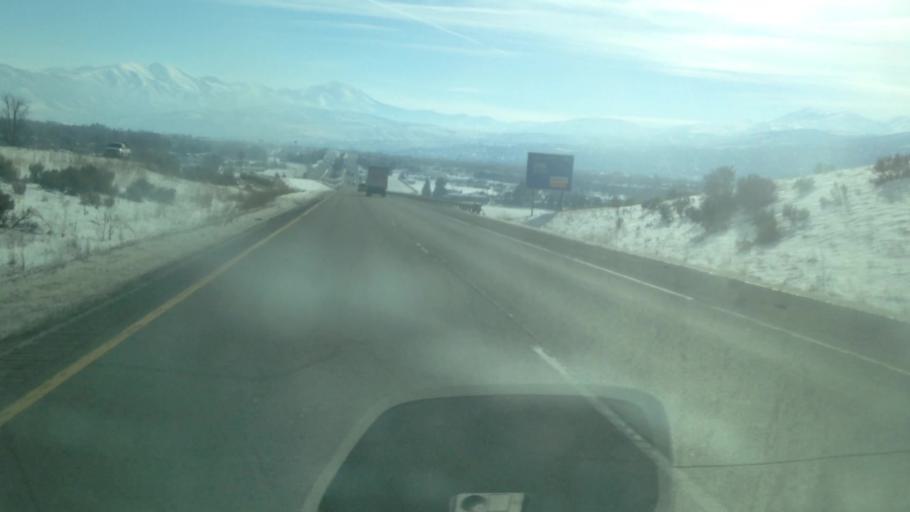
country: US
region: Idaho
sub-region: Bannock County
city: Pocatello
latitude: 42.8505
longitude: -112.4150
